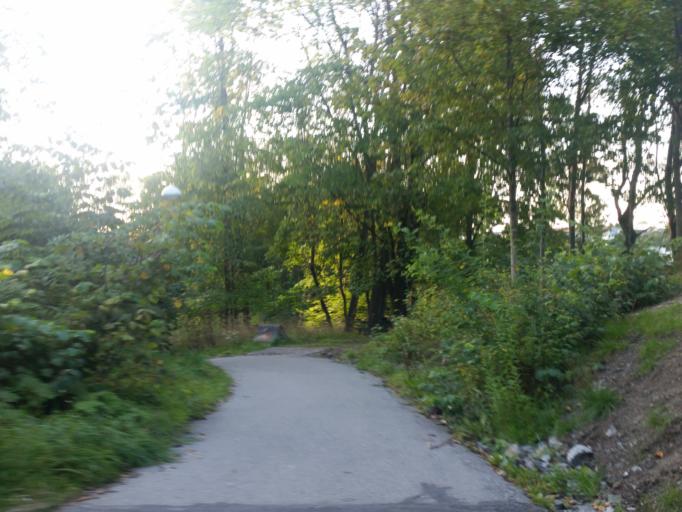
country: SE
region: Stockholm
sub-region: Stockholms Kommun
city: Arsta
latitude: 59.3006
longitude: 18.0791
